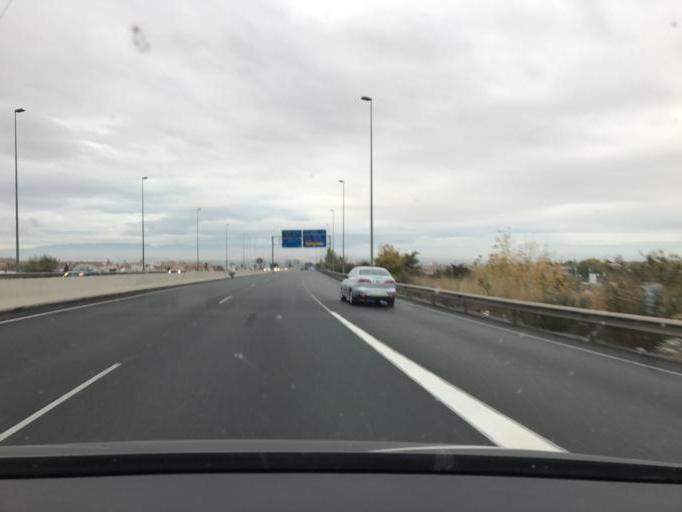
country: ES
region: Andalusia
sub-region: Provincia de Granada
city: Maracena
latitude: 37.2077
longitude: -3.6240
